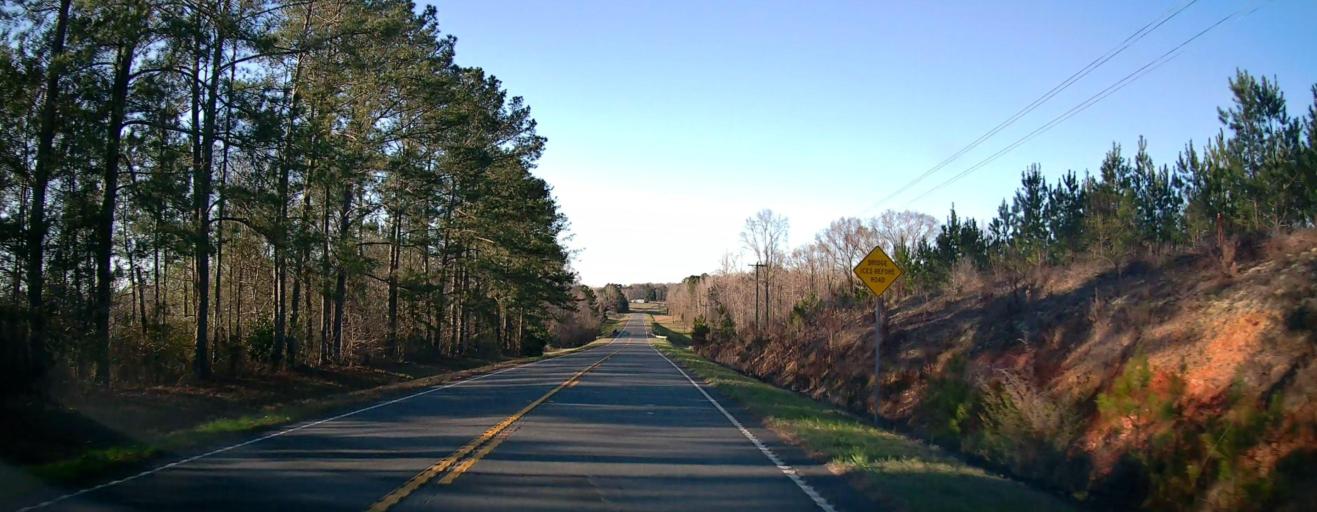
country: US
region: Georgia
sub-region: Talbot County
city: Talbotton
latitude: 32.5902
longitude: -84.5546
